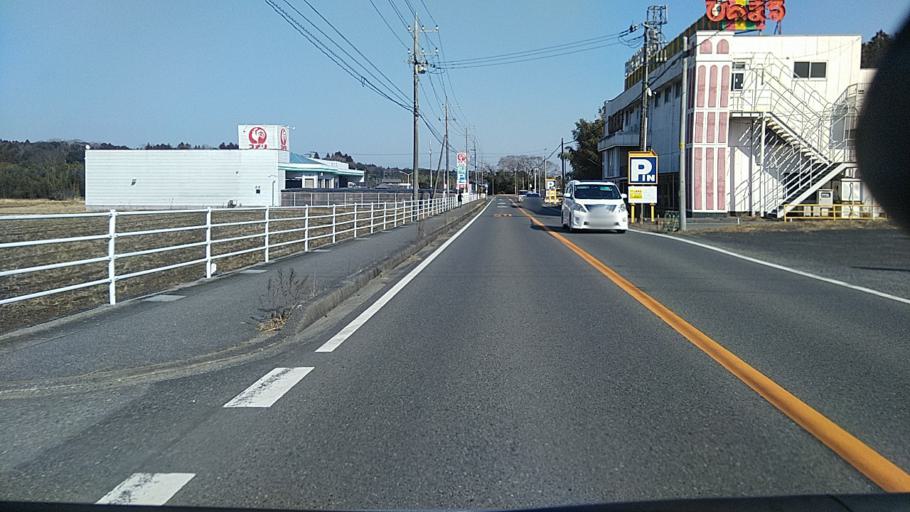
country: JP
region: Chiba
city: Mobara
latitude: 35.4058
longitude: 140.2389
